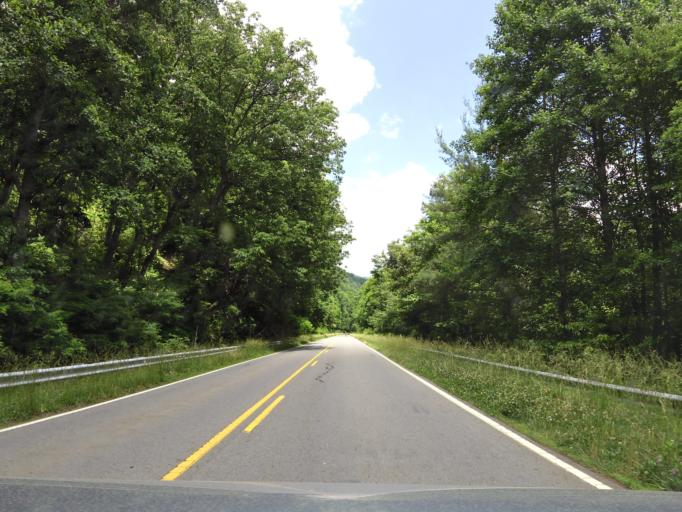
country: US
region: North Carolina
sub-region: Graham County
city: Robbinsville
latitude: 35.3673
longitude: -83.8579
